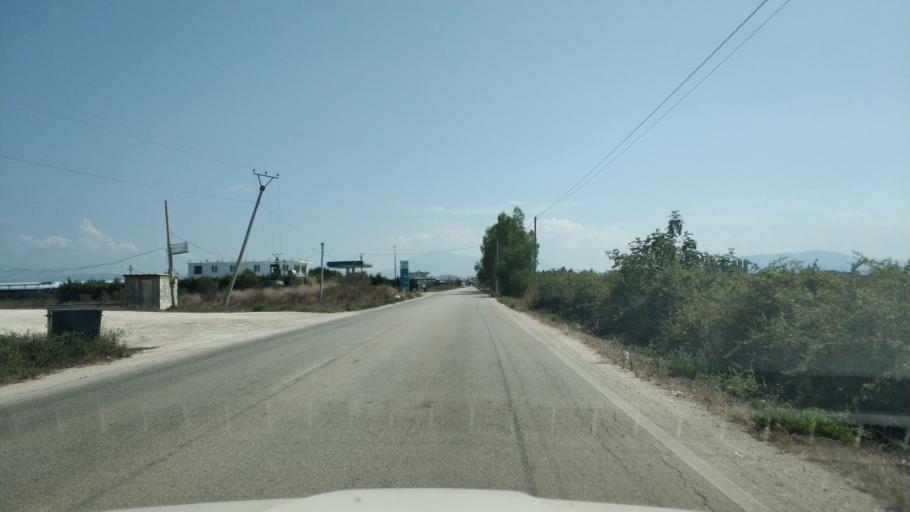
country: AL
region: Fier
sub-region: Rrethi i Lushnjes
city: Krutja e Poshtme
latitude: 40.8823
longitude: 19.6607
